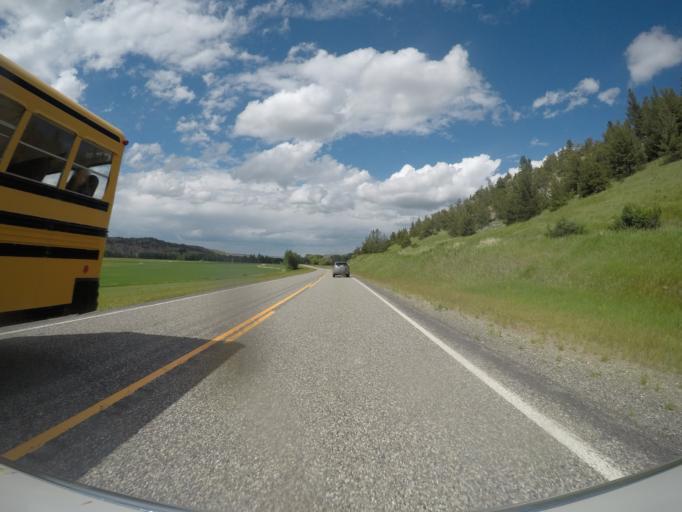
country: US
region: Montana
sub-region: Sweet Grass County
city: Big Timber
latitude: 45.7168
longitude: -109.9985
